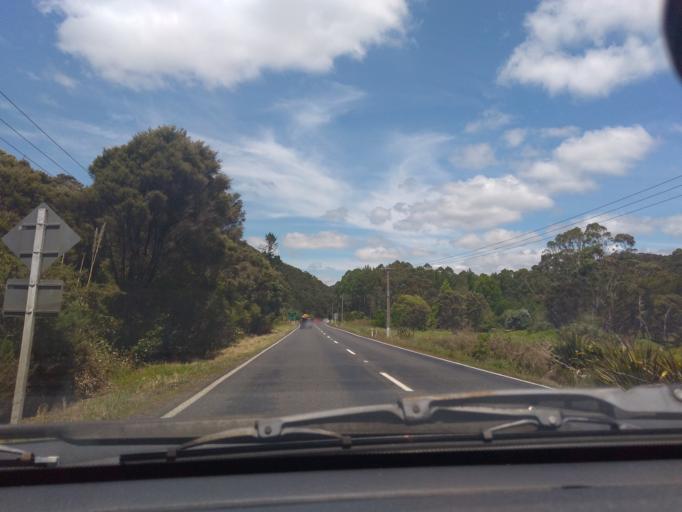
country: NZ
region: Northland
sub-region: Far North District
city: Kerikeri
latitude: -35.0839
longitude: 173.7631
